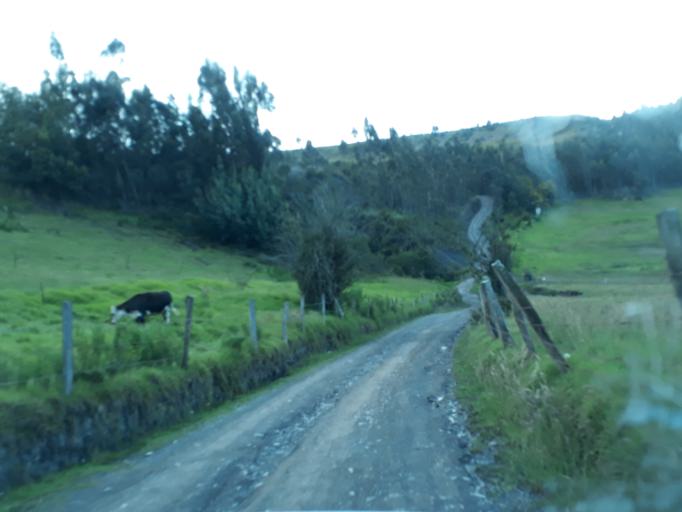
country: CO
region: Cundinamarca
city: Carmen de Carupa
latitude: 5.3380
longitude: -73.9070
